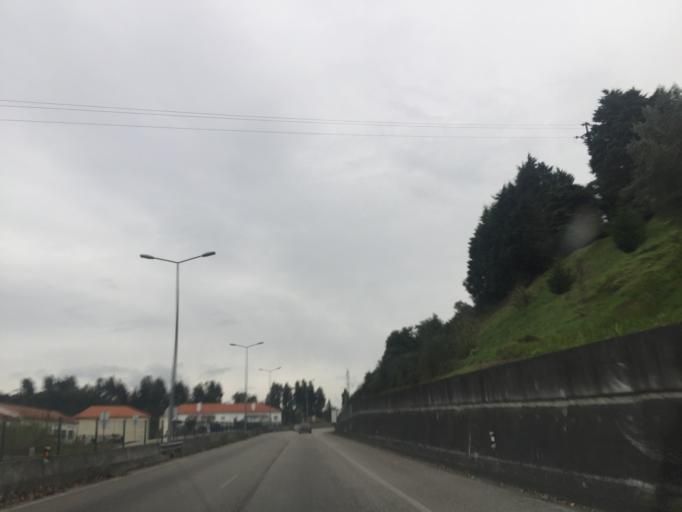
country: PT
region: Coimbra
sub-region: Coimbra
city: Coimbra
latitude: 40.1903
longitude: -8.4304
